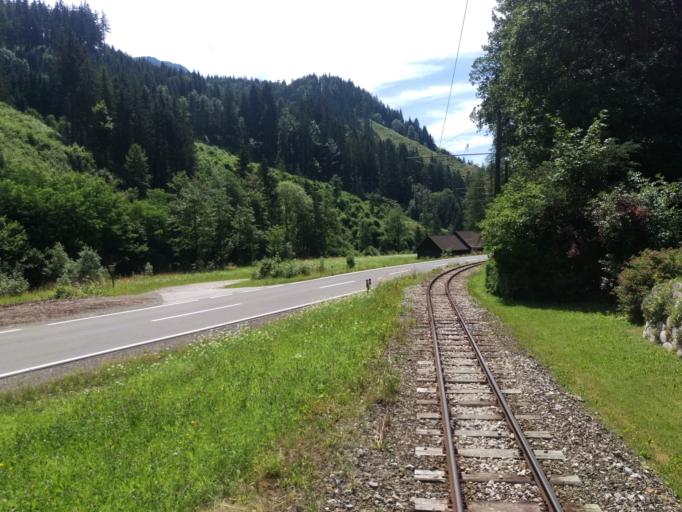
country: AT
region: Styria
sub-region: Politischer Bezirk Bruck-Muerzzuschlag
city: Pernegg an der Mur
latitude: 47.3823
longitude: 15.4049
